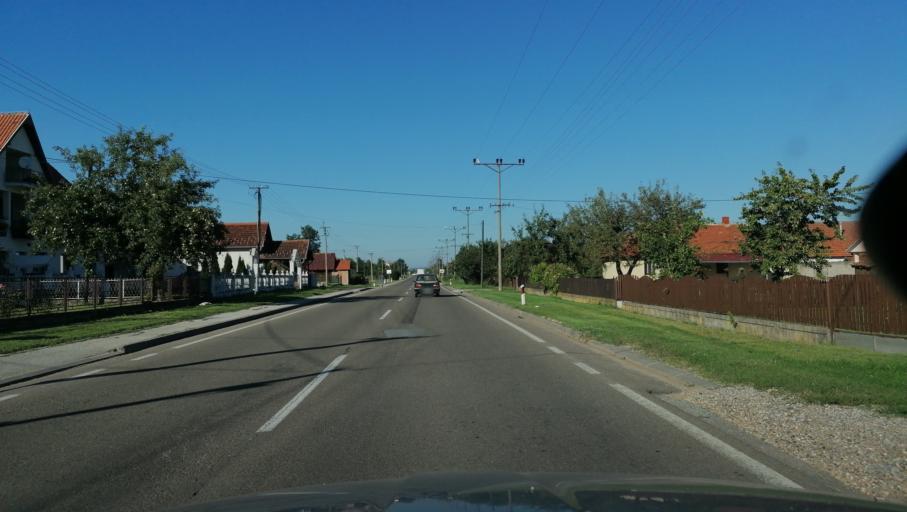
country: RS
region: Central Serbia
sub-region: Sumadijski Okrug
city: Knic
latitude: 43.9041
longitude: 20.6316
